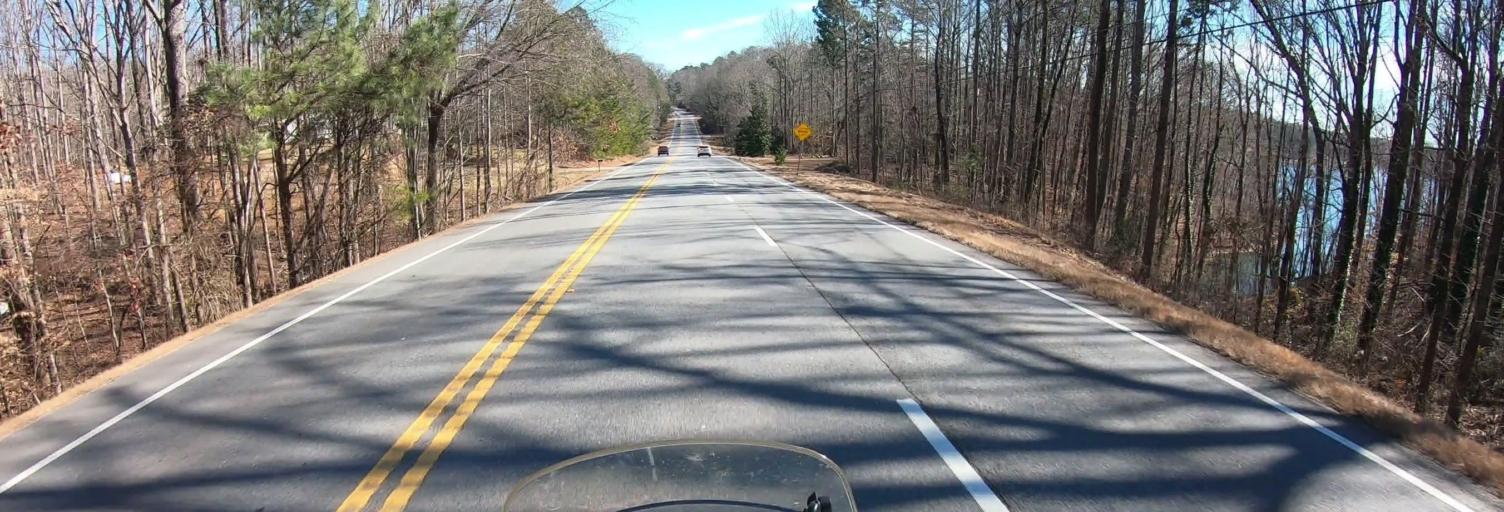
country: US
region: Georgia
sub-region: Forsyth County
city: Cumming
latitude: 34.2475
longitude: -84.0291
